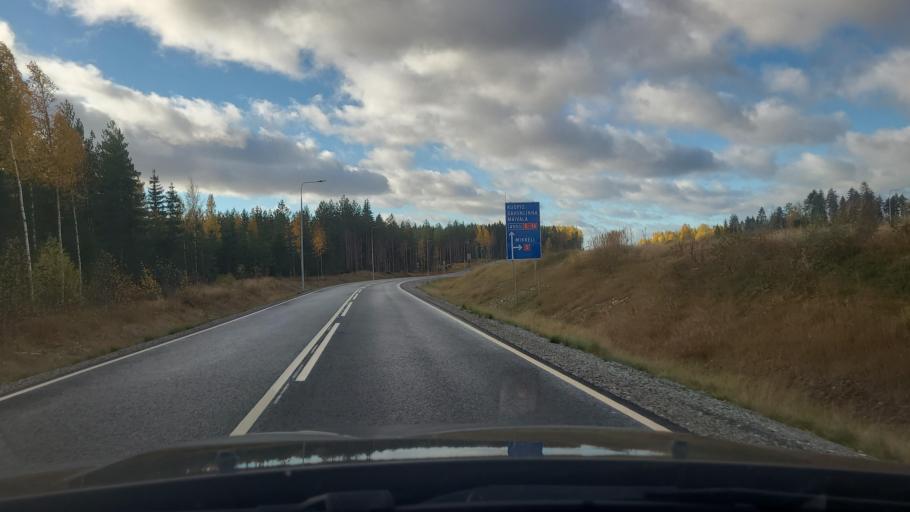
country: FI
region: Southern Savonia
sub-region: Pieksaemaeki
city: Juva
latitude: 61.8318
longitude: 27.6561
